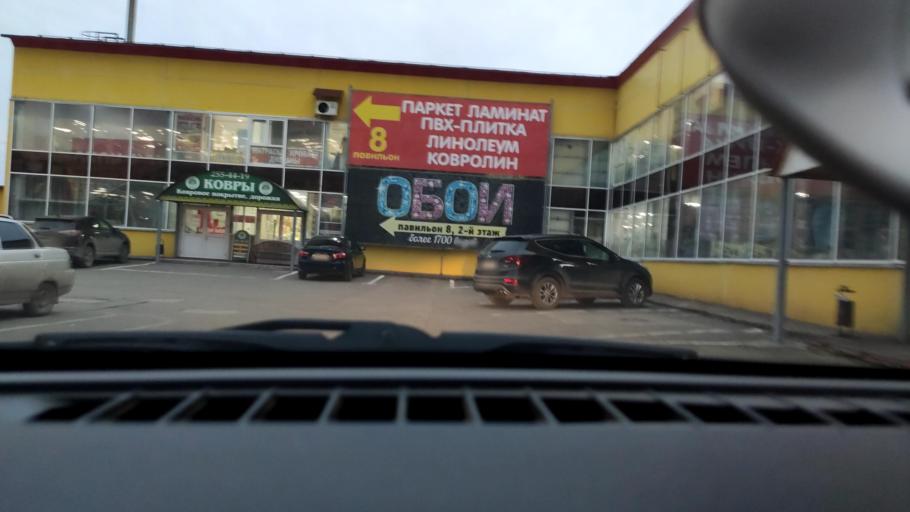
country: RU
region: Perm
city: Kondratovo
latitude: 58.0018
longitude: 56.1446
